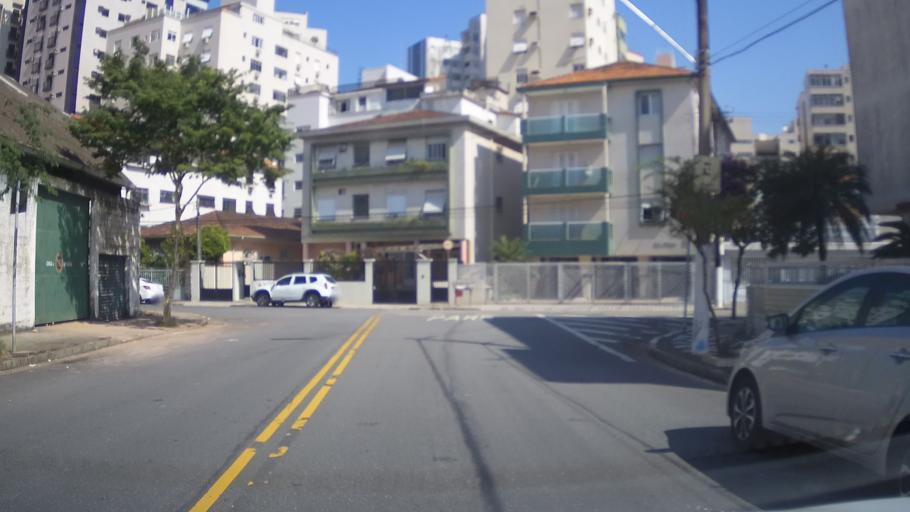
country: BR
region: Sao Paulo
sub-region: Santos
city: Santos
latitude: -23.9889
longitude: -46.3061
